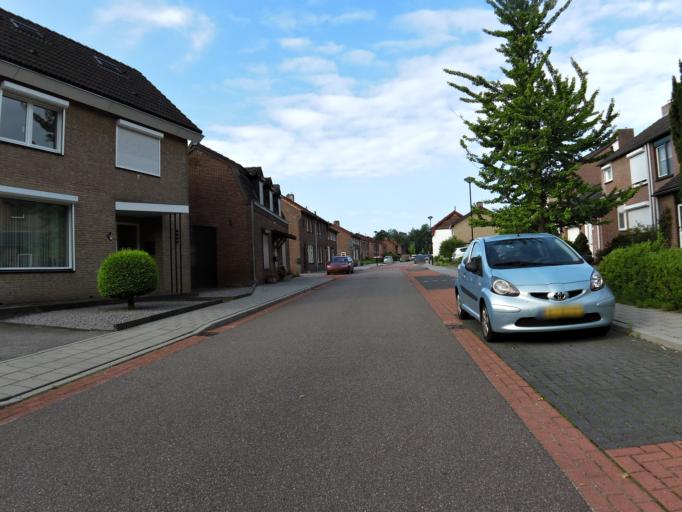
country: NL
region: Limburg
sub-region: Gemeente Schinnen
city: Schinnen
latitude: 50.9406
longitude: 5.8795
